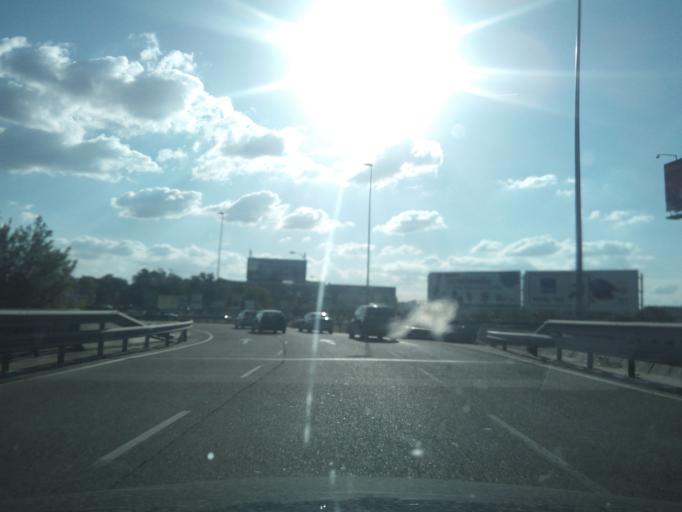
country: ES
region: Madrid
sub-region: Provincia de Madrid
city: San Sebastian de los Reyes
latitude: 40.5477
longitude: -3.6081
